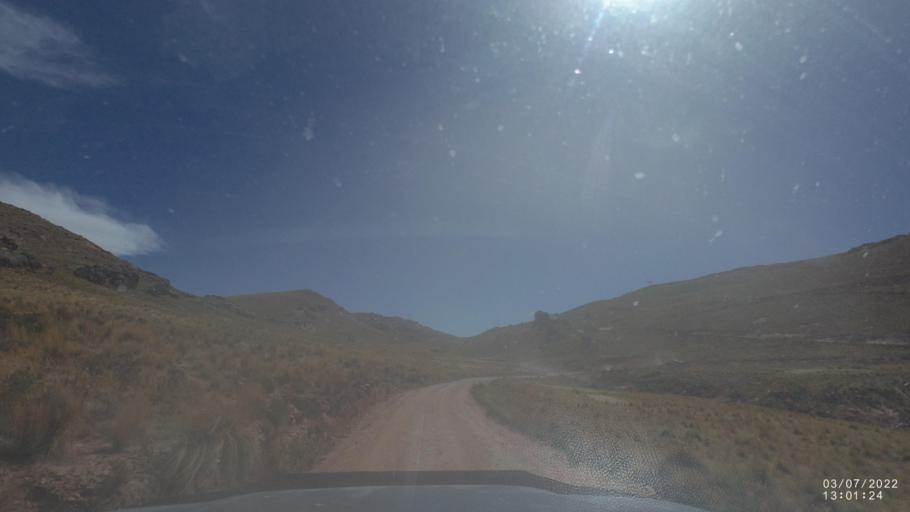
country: BO
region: Cochabamba
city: Colchani
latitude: -17.7091
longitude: -66.6912
